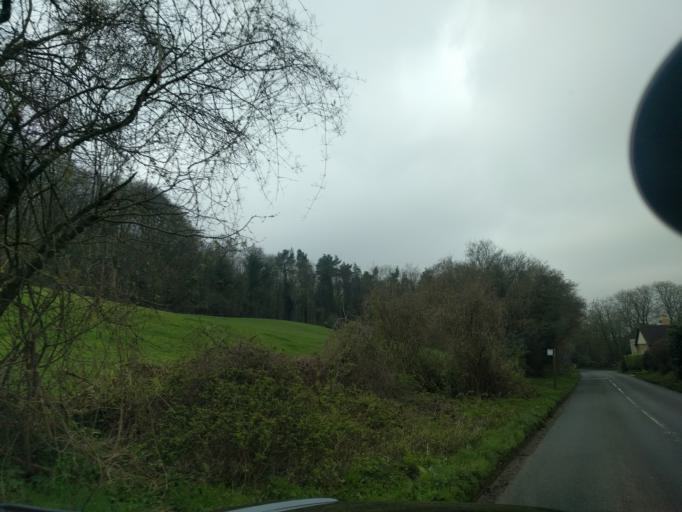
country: GB
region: England
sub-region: Wiltshire
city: Box
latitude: 51.4008
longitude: -2.2816
